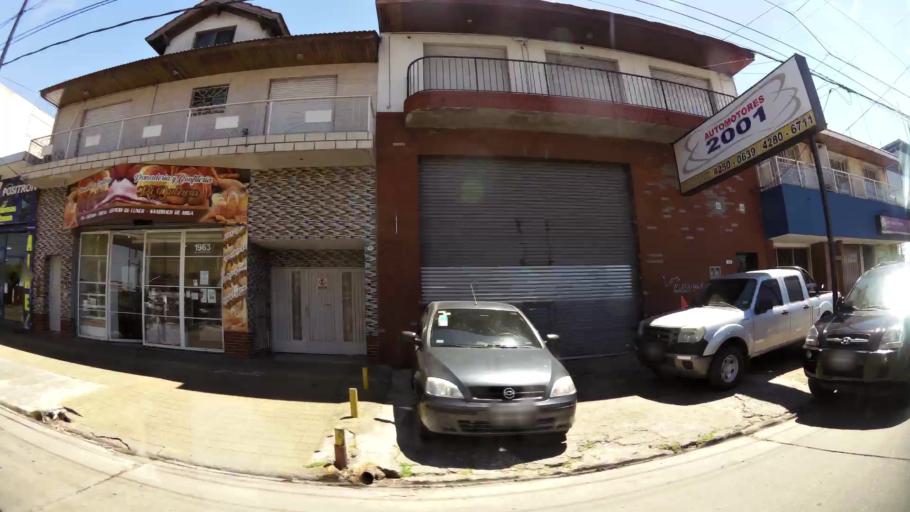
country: AR
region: Buenos Aires
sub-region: Partido de Quilmes
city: Quilmes
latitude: -34.7370
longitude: -58.2783
